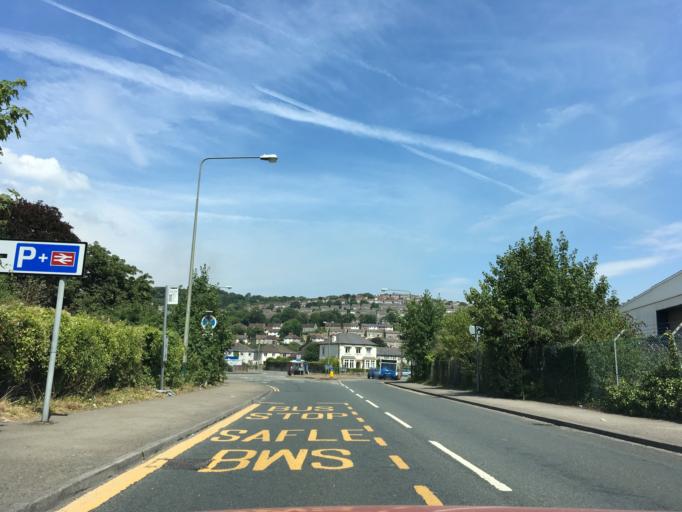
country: GB
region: Wales
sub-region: Caerphilly County Borough
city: Risca
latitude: 51.6020
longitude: -3.0922
